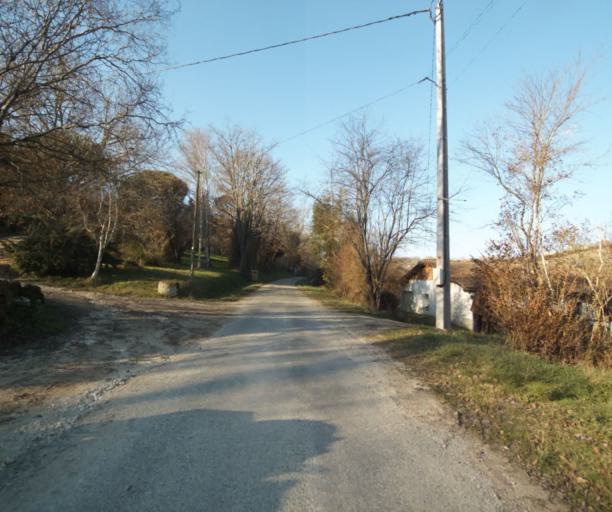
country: FR
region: Midi-Pyrenees
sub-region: Departement du Tarn-et-Garonne
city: Moissac
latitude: 44.1312
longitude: 1.0887
